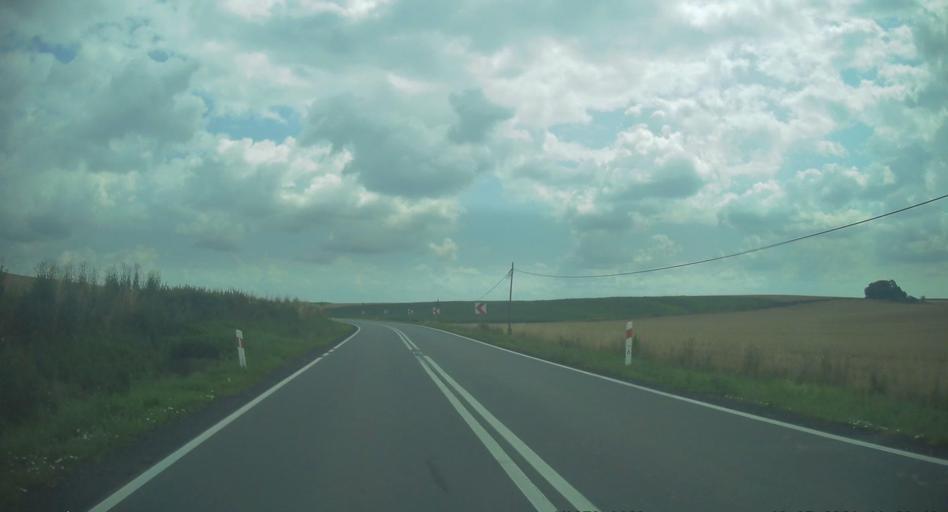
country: PL
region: Opole Voivodeship
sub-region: Powiat prudnicki
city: Raclawice Slaskie
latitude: 50.3518
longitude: 17.8094
